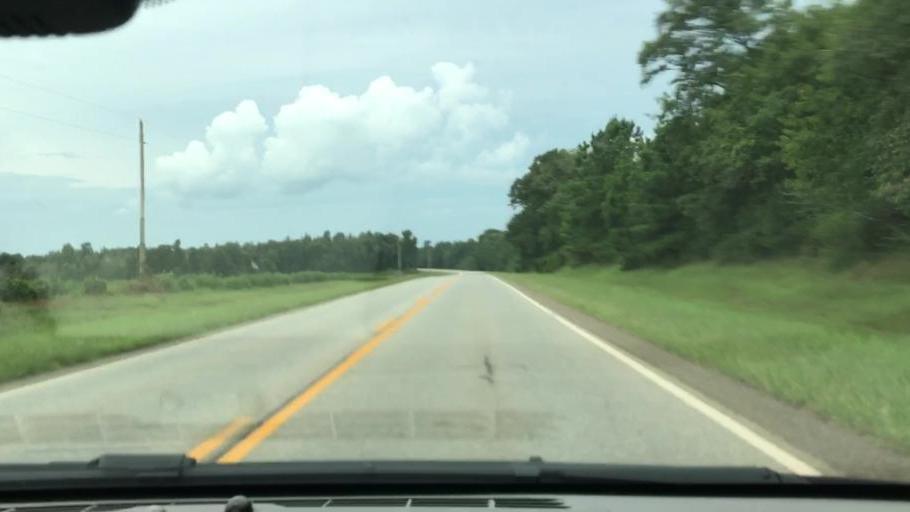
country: US
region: Georgia
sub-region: Early County
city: Blakely
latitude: 31.3154
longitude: -85.0388
